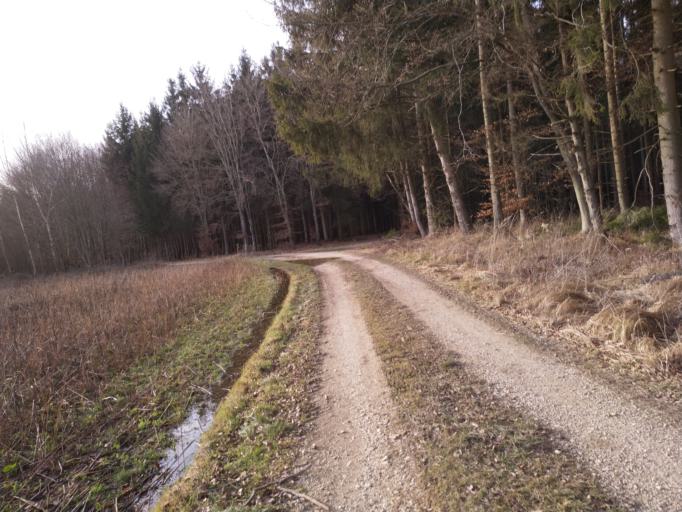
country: DE
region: Bavaria
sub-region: Swabia
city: Rettenbach
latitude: 48.4290
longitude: 10.3201
